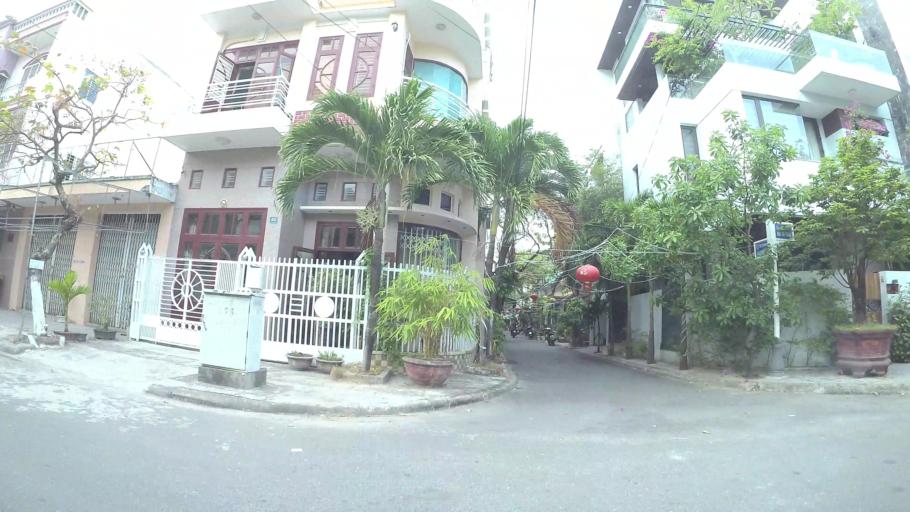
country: VN
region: Da Nang
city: Son Tra
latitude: 16.0525
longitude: 108.2343
